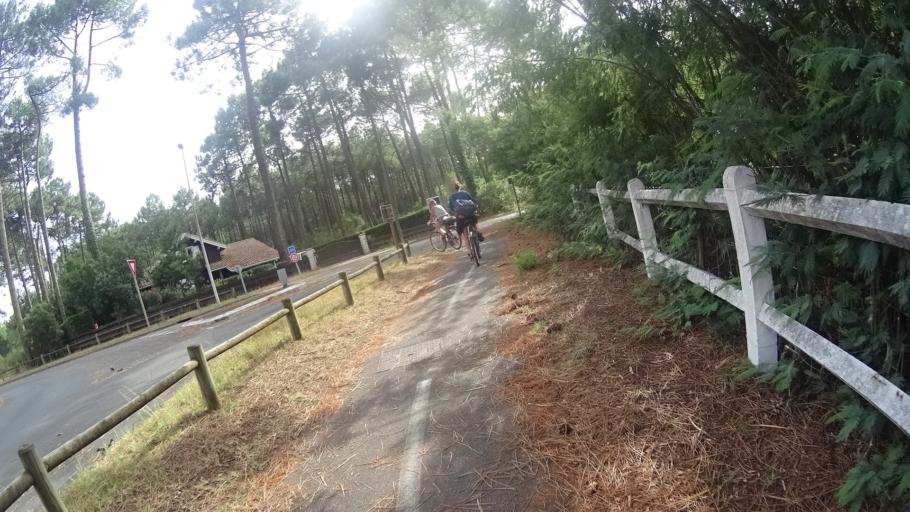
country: FR
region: Aquitaine
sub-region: Departement de la Gironde
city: Lacanau
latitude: 44.9927
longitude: -1.1467
